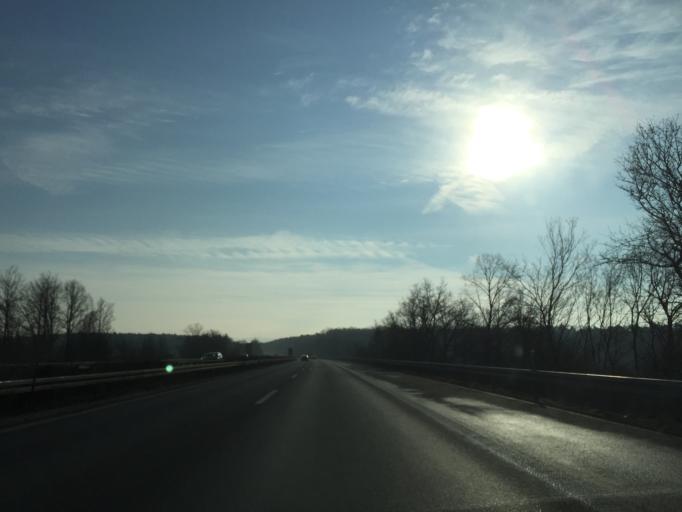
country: DE
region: Bavaria
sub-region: Regierungsbezirk Unterfranken
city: Kleinlangheim
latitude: 49.7780
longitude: 10.3028
